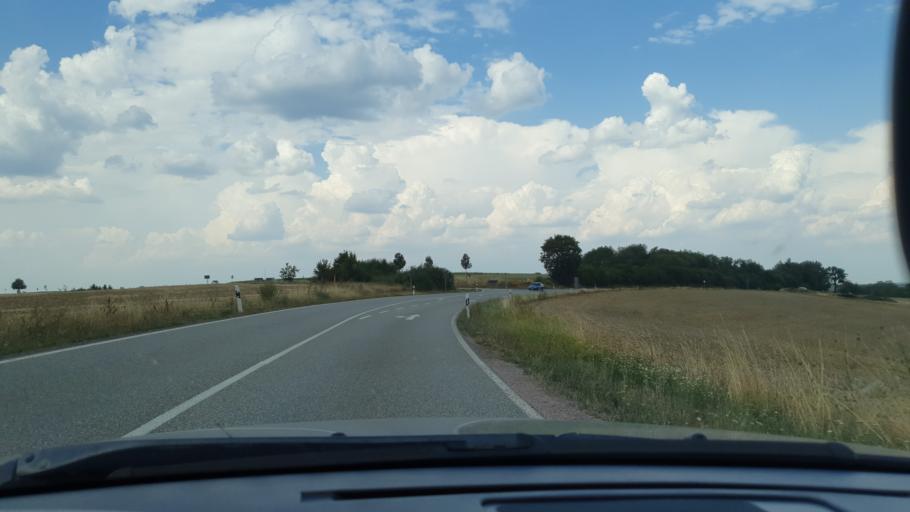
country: DE
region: Rheinland-Pfalz
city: Zweibrucken
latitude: 49.2795
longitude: 7.3739
